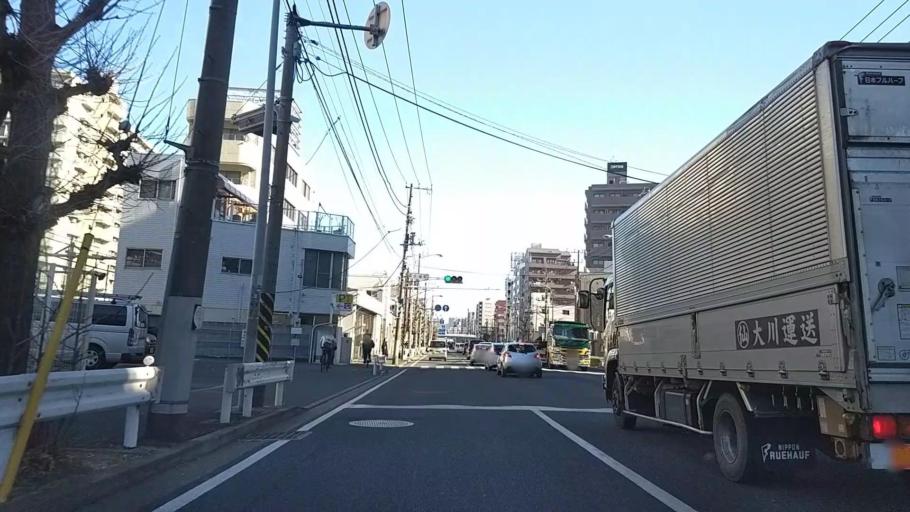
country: JP
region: Kanagawa
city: Yokohama
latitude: 35.4510
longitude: 139.6050
